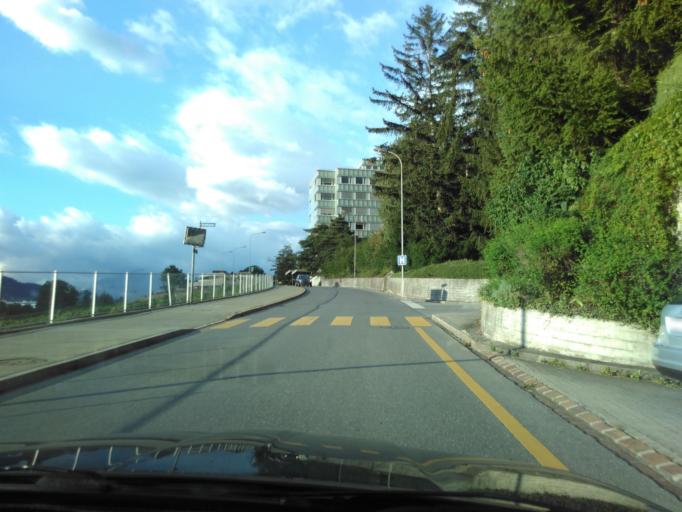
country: CH
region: Grisons
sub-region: Plessur District
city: Chur
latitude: 46.8600
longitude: 9.5408
